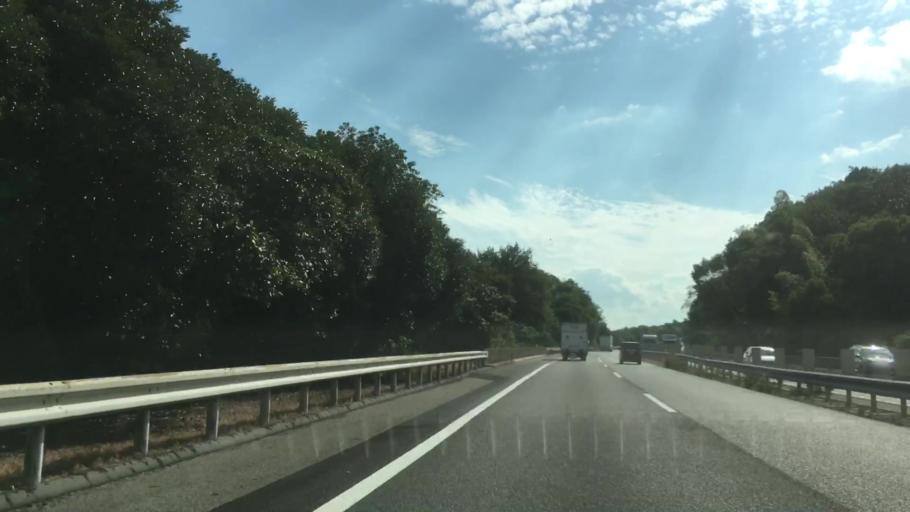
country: JP
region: Hiroshima
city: Ono-hara
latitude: 34.2811
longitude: 132.2592
